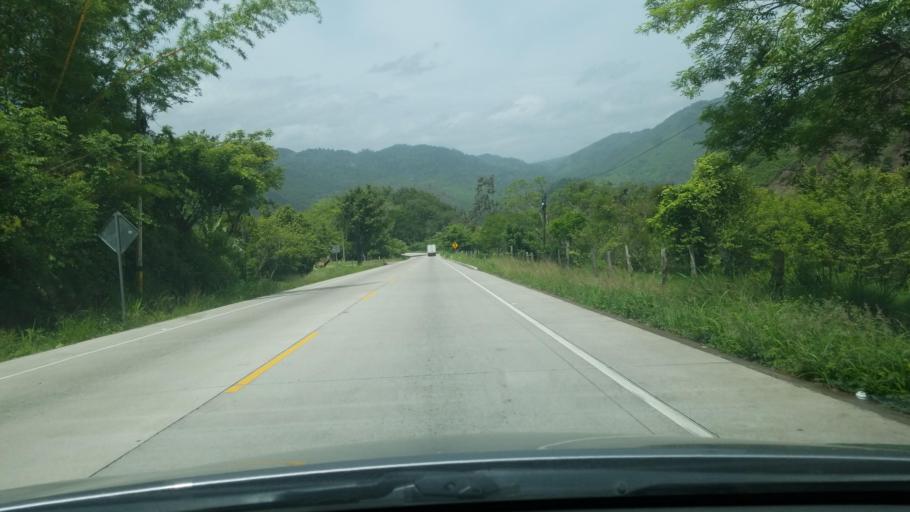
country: HN
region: Copan
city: Quezailica
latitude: 14.9064
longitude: -88.7536
